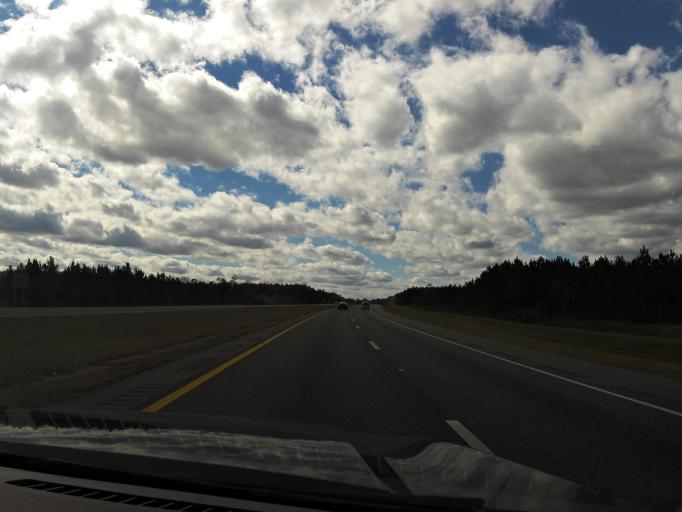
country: US
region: Florida
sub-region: Bradford County
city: Starke
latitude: 29.9914
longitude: -82.0985
